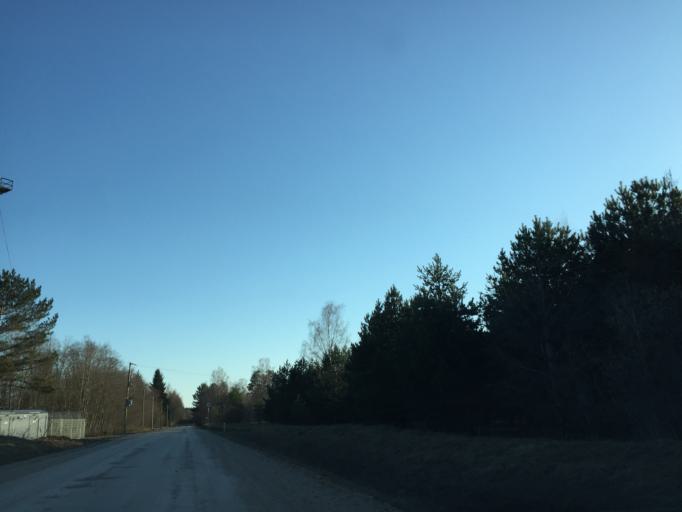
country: EE
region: Ida-Virumaa
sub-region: Sillamaee linn
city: Sillamae
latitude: 59.0941
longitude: 27.7882
